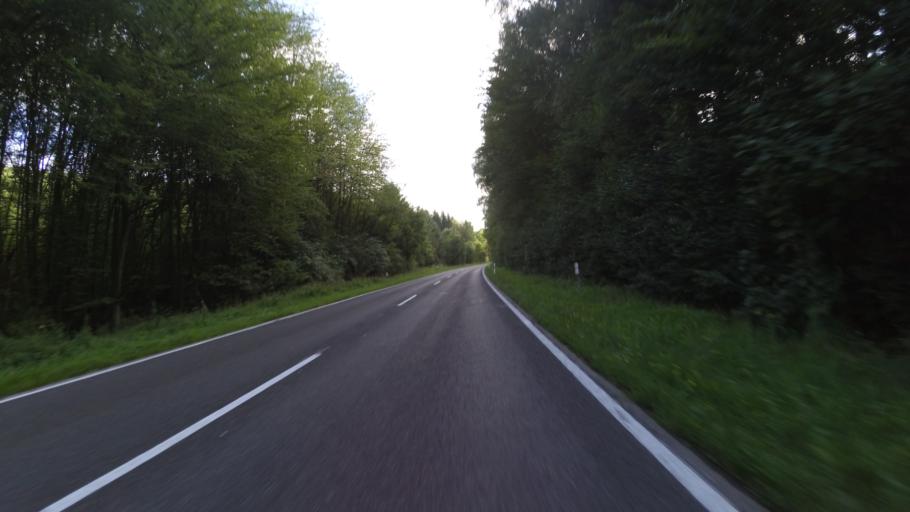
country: DE
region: Saarland
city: Nonnweiler
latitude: 49.5748
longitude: 6.9769
